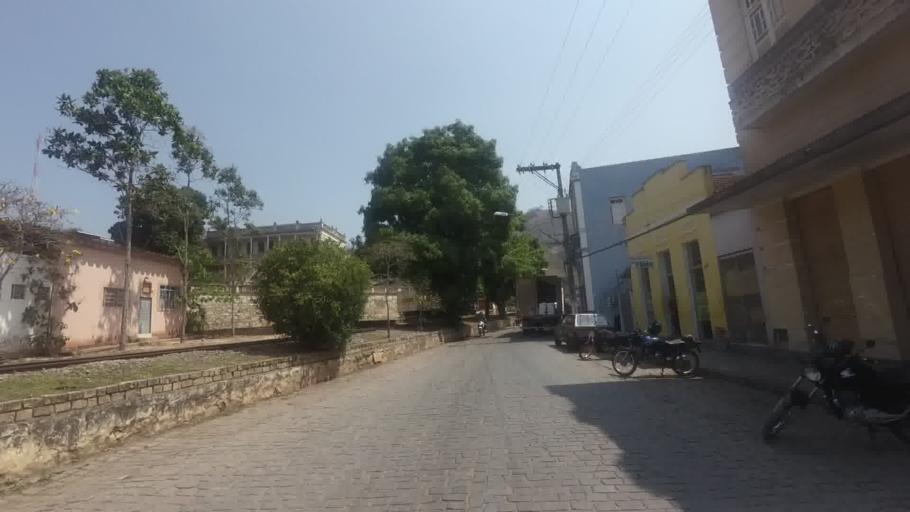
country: BR
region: Espirito Santo
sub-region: Mimoso Do Sul
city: Mimoso do Sul
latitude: -20.9546
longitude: -41.3508
